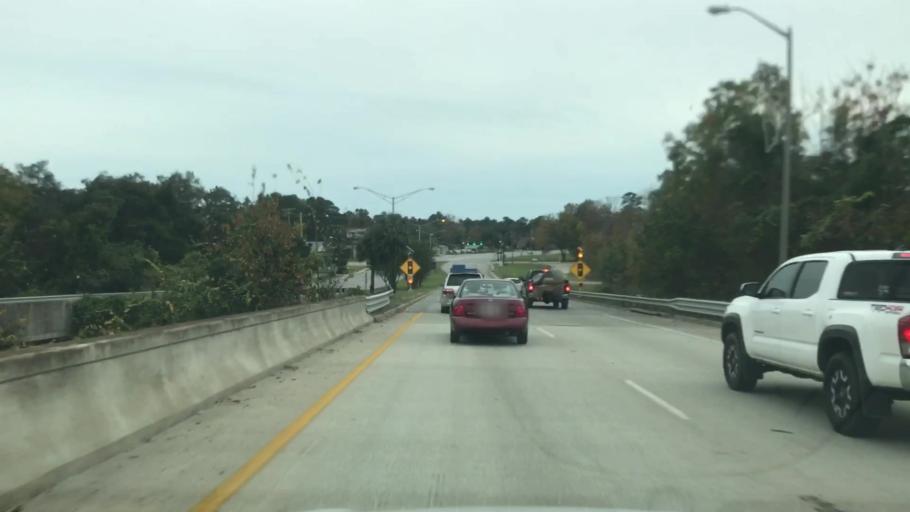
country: US
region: South Carolina
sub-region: Georgetown County
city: Georgetown
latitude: 33.3549
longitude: -79.2935
